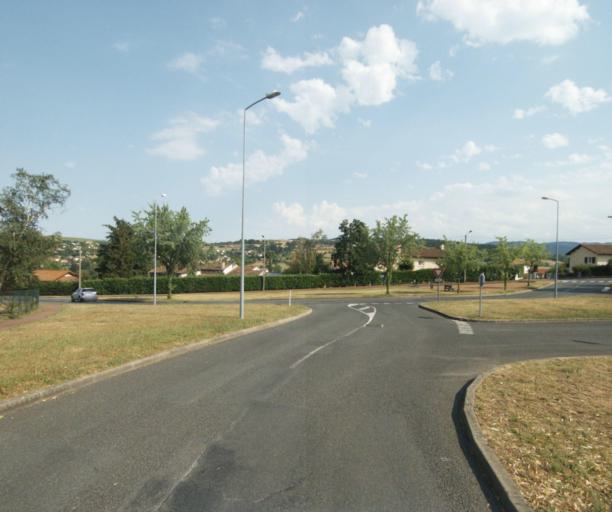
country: FR
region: Rhone-Alpes
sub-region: Departement du Rhone
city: Saint-Germain-Nuelles
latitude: 45.8328
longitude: 4.6086
